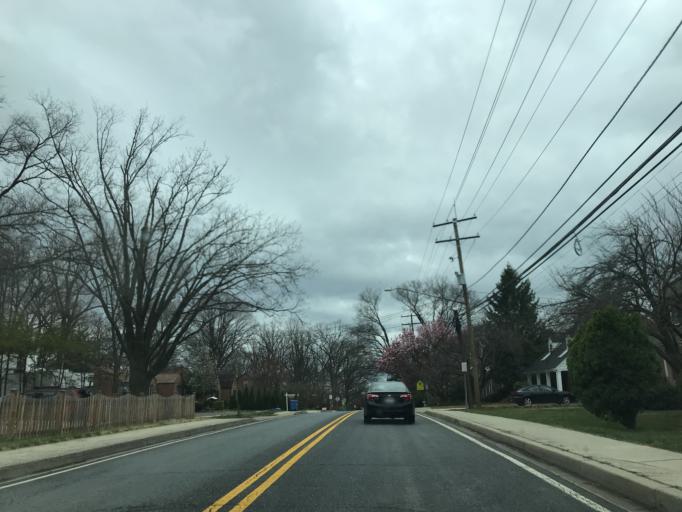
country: US
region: Maryland
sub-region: Montgomery County
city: Four Corners
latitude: 39.0044
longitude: -77.0063
